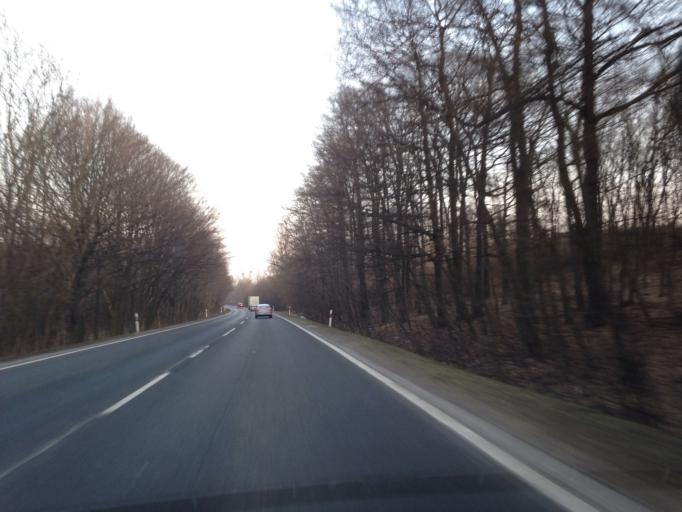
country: HU
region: Fejer
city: Szarliget
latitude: 47.5047
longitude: 18.4936
